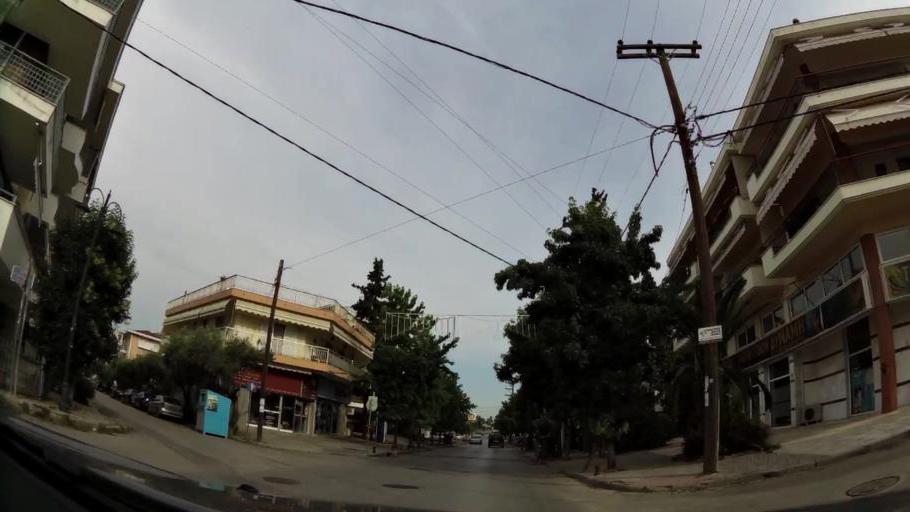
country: GR
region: Central Macedonia
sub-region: Nomos Thessalonikis
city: Thermi
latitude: 40.5514
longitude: 23.0198
